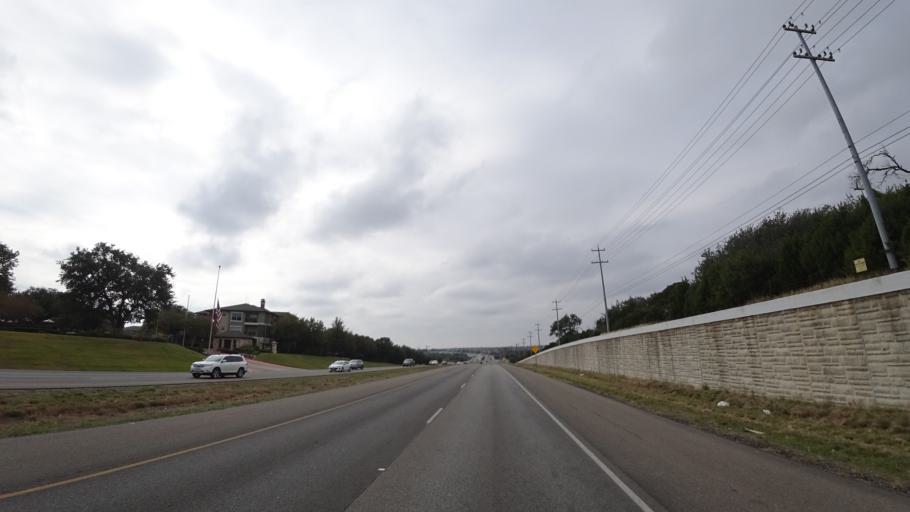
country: US
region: Texas
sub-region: Williamson County
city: Brushy Creek
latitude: 30.5115
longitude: -97.7744
